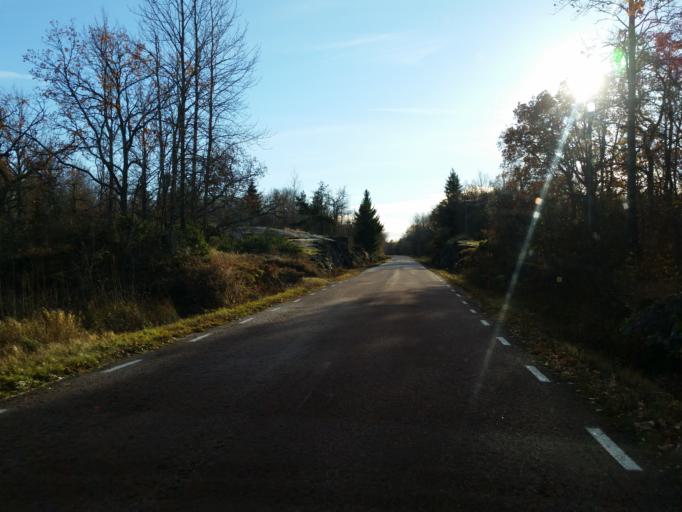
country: AX
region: Alands skaergard
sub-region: Kumlinge
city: Kumlinge
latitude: 60.2477
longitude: 20.7325
